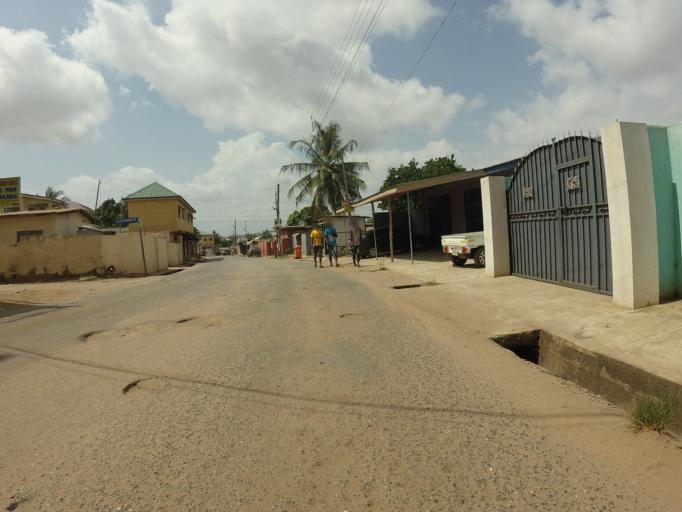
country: GH
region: Greater Accra
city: Dome
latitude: 5.6156
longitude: -0.2475
